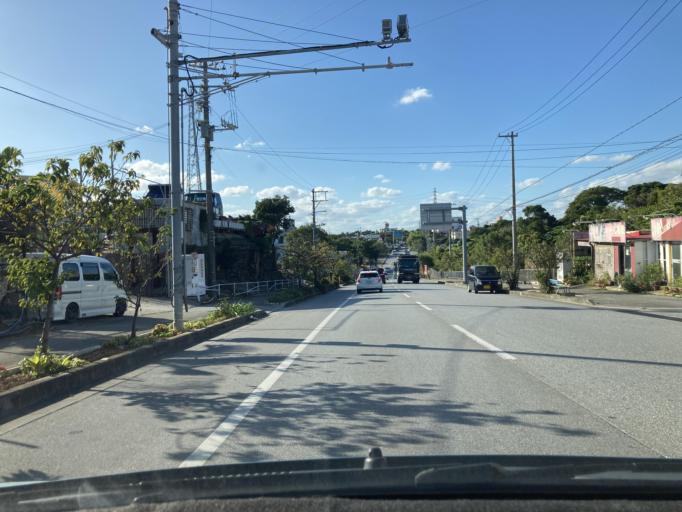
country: JP
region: Okinawa
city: Okinawa
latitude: 26.3739
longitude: 127.8245
